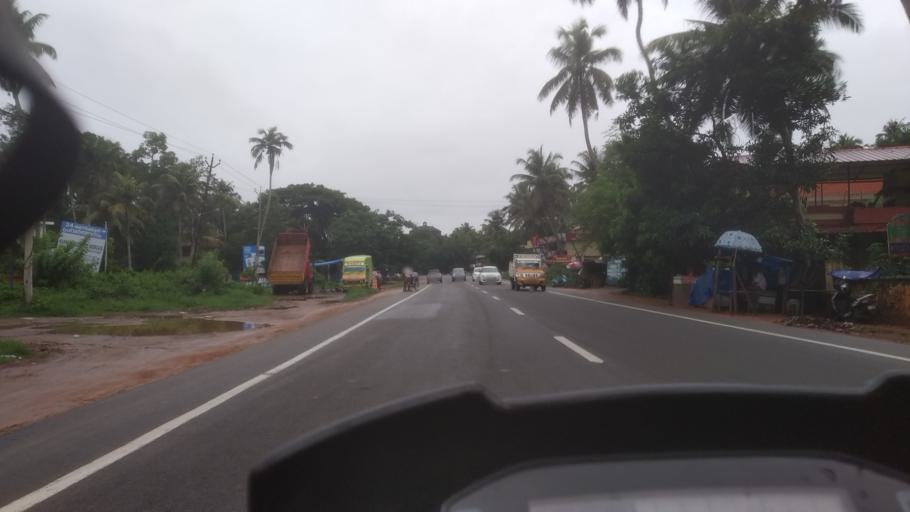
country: IN
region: Kerala
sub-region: Alappuzha
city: Kayankulam
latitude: 9.1586
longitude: 76.5086
